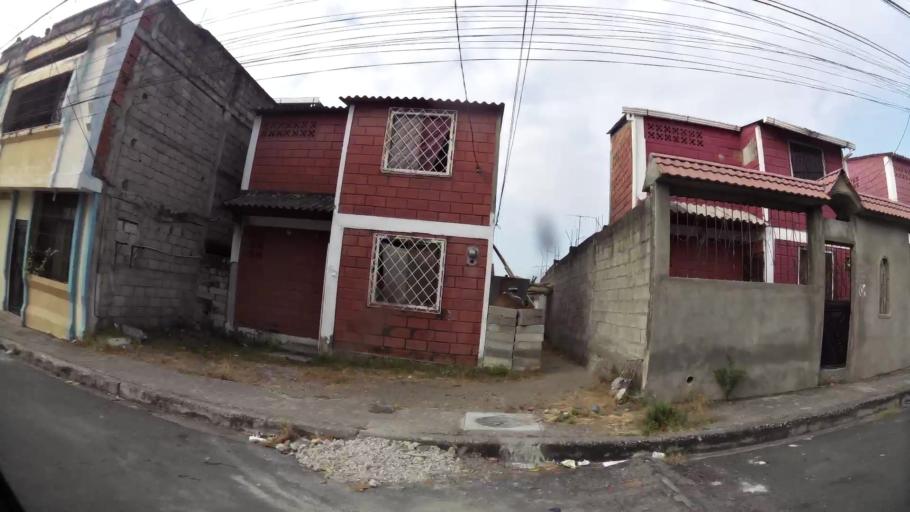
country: EC
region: Guayas
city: Eloy Alfaro
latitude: -2.1324
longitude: -79.8919
